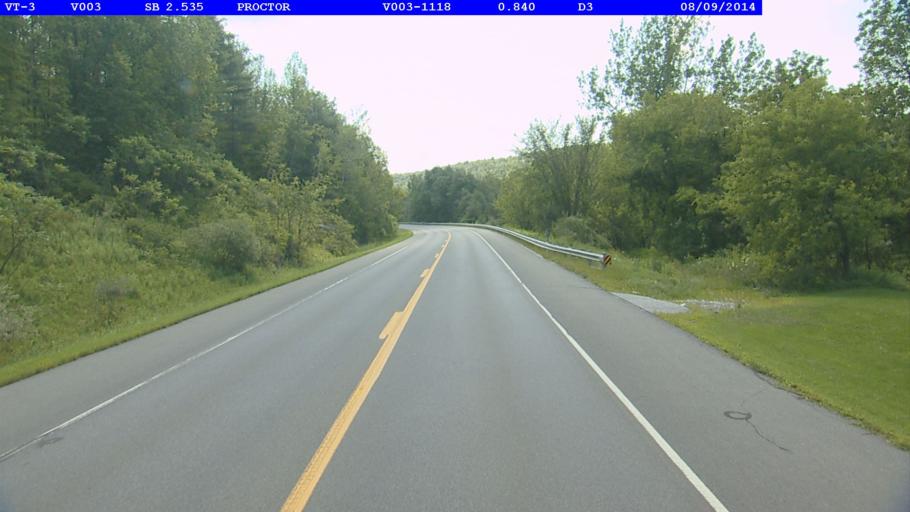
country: US
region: Vermont
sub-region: Rutland County
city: West Rutland
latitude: 43.6360
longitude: -73.0343
